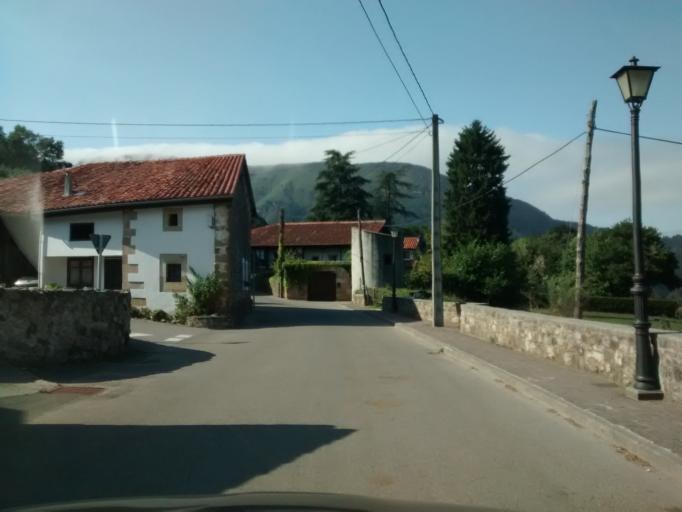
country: ES
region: Cantabria
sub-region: Provincia de Cantabria
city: Ruente
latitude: 43.2593
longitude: -4.2471
